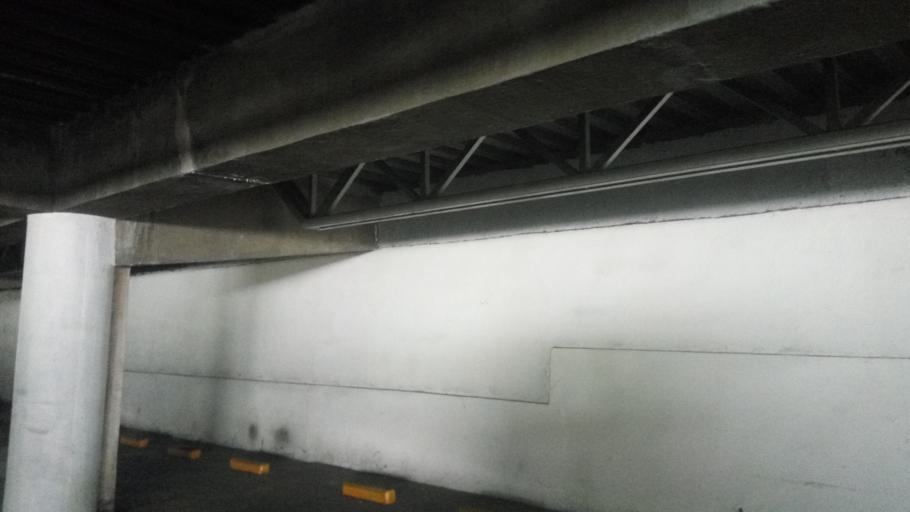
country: MX
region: Tabasco
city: Villahermosa
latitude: 17.9938
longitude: -92.9396
